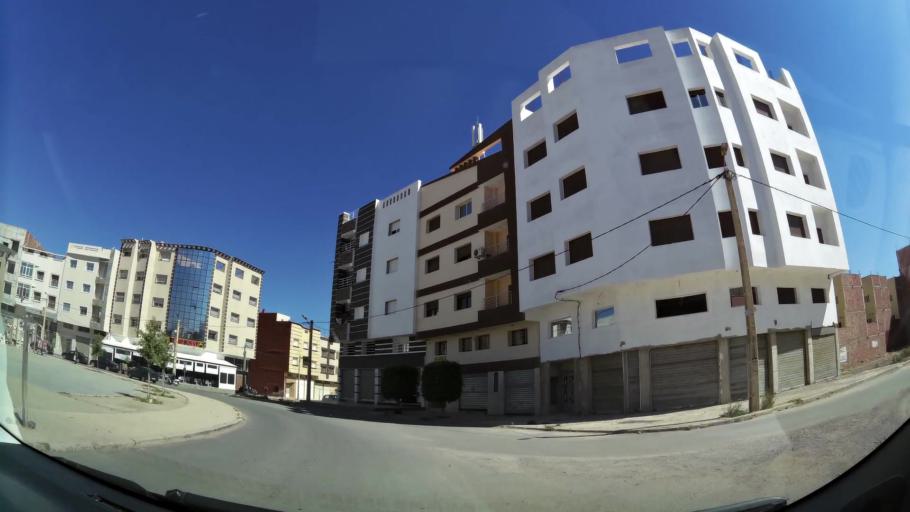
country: MA
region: Oriental
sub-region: Oujda-Angad
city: Oujda
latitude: 34.6607
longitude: -1.8878
